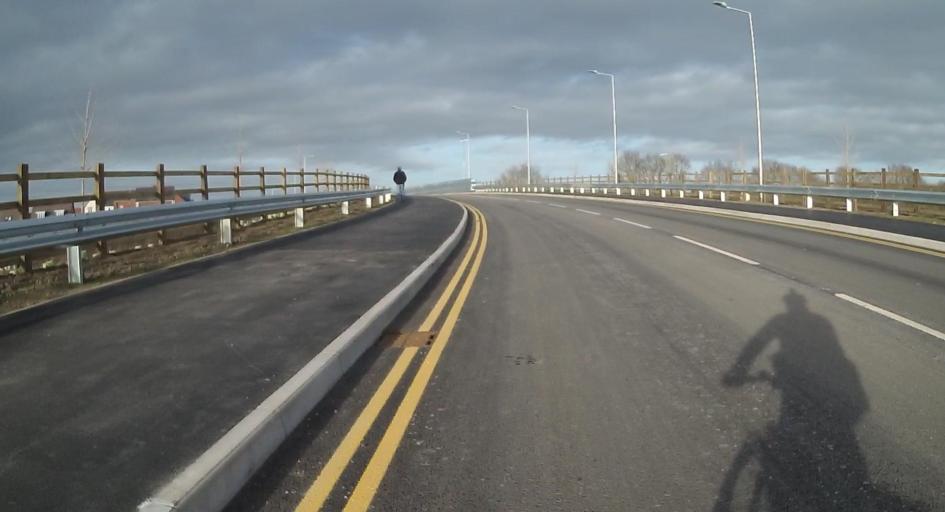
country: GB
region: England
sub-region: Wokingham
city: Wokingham
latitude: 51.4057
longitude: -0.8065
